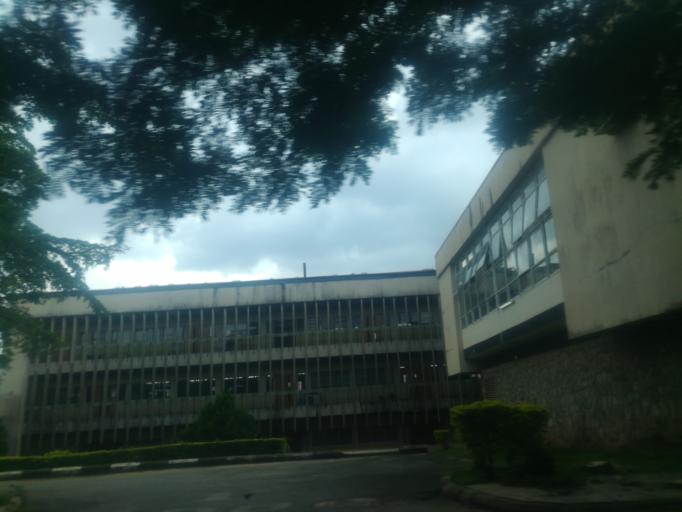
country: NG
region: Oyo
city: Ibadan
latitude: 7.4456
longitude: 3.8942
